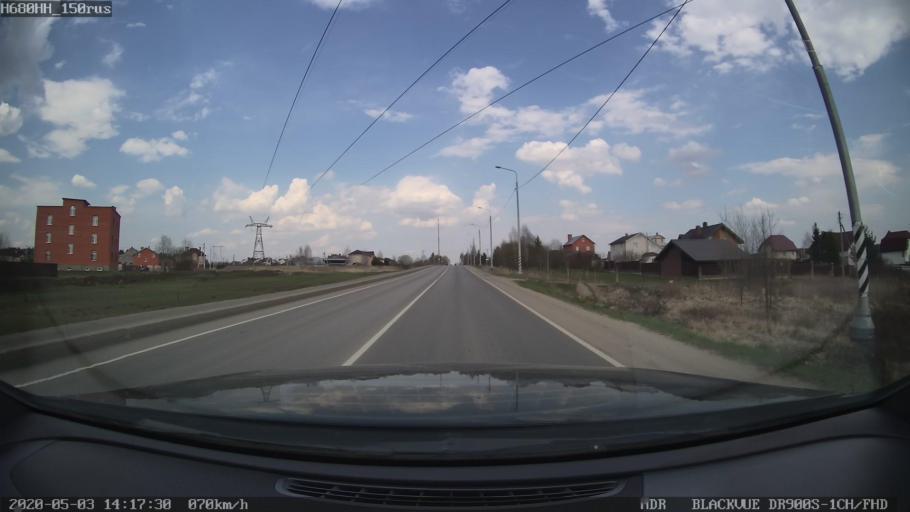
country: RU
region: Moskovskaya
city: Solnechnogorsk
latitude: 56.2094
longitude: 36.9651
